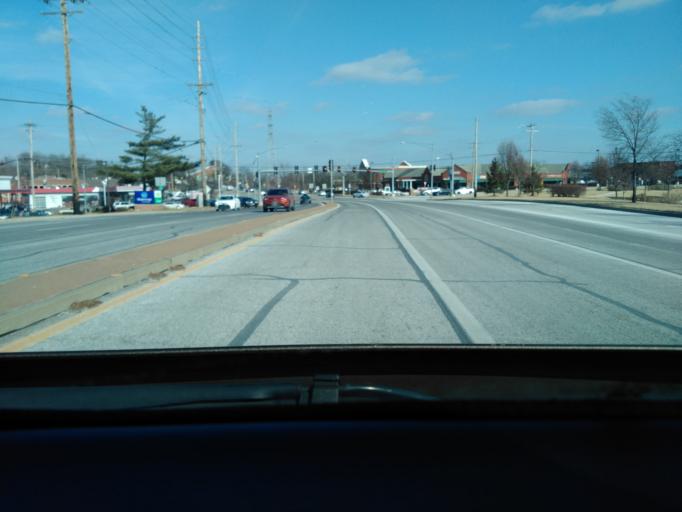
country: US
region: Missouri
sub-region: Saint Louis County
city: Manchester
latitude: 38.6235
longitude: -90.5170
